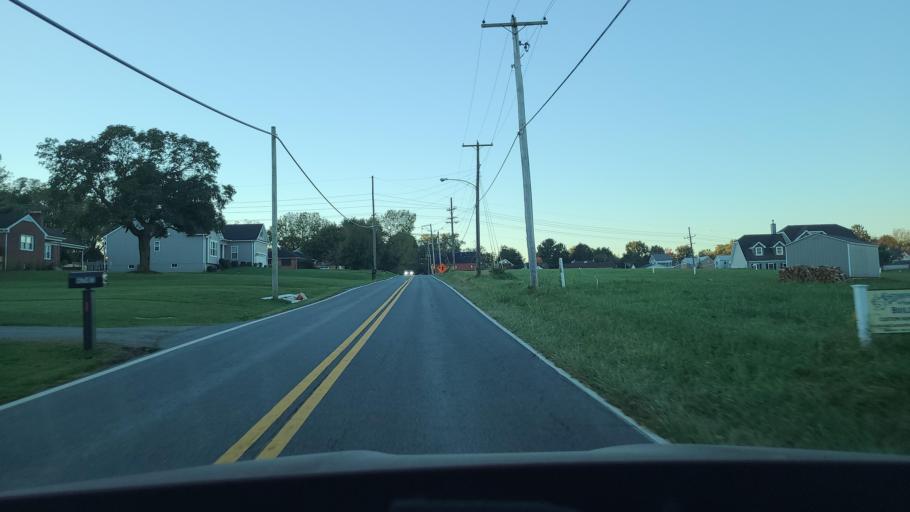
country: US
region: Maryland
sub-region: Frederick County
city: Jefferson
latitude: 39.3641
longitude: -77.5382
